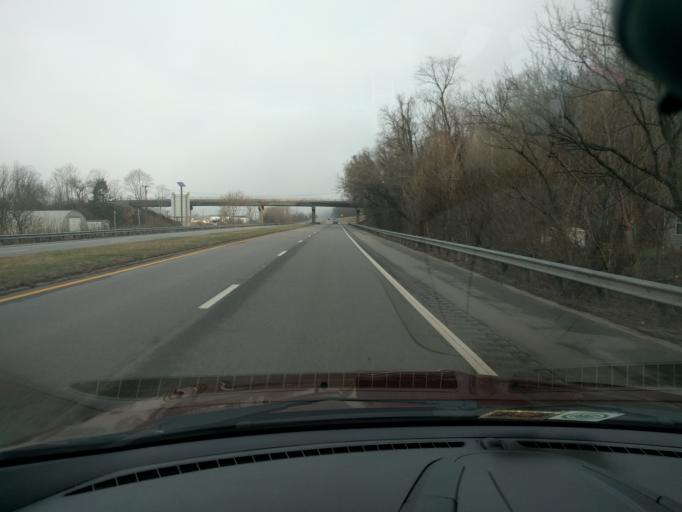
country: US
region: West Virginia
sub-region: Kanawha County
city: Chesapeake
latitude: 38.2240
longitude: -81.5277
